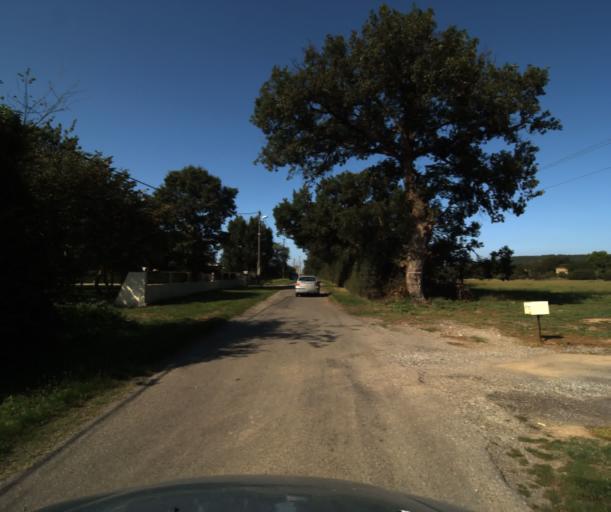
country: FR
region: Midi-Pyrenees
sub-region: Departement de la Haute-Garonne
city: Le Fauga
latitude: 43.4189
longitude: 1.3059
